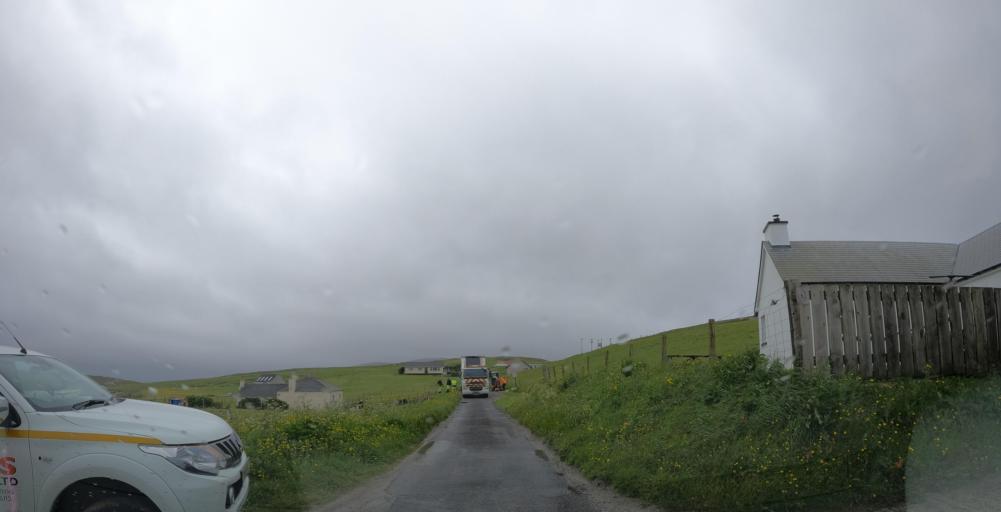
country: GB
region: Scotland
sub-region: Eilean Siar
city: Barra
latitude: 57.0362
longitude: -7.4275
